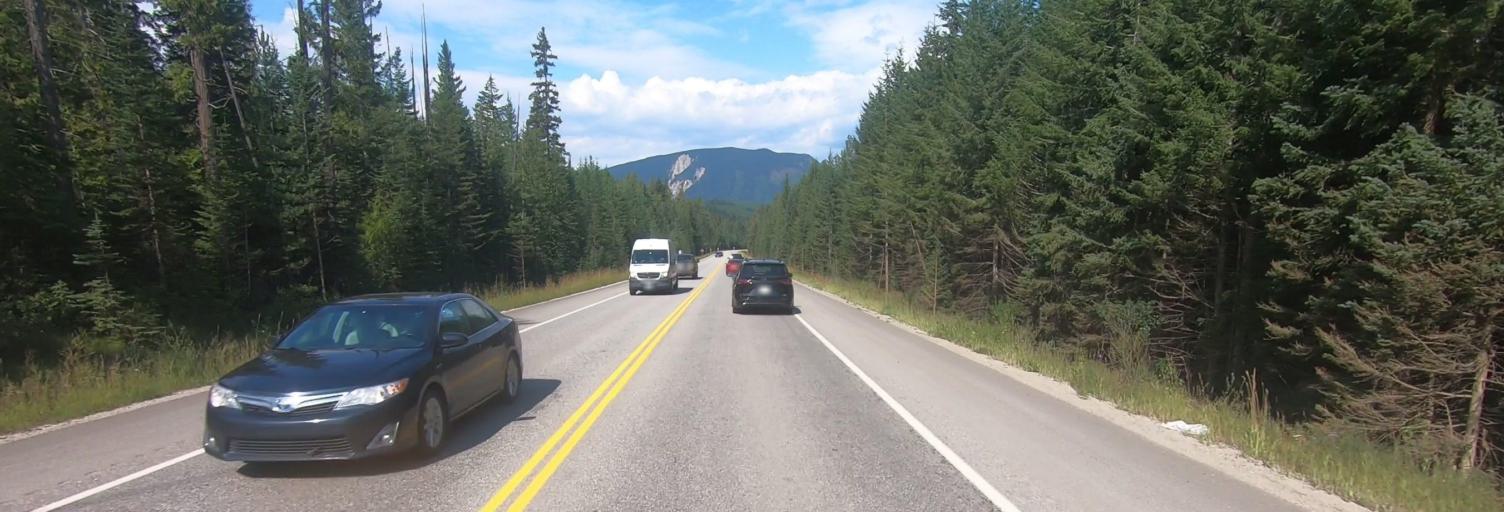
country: CA
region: British Columbia
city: Golden
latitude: 51.4899
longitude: -117.3896
